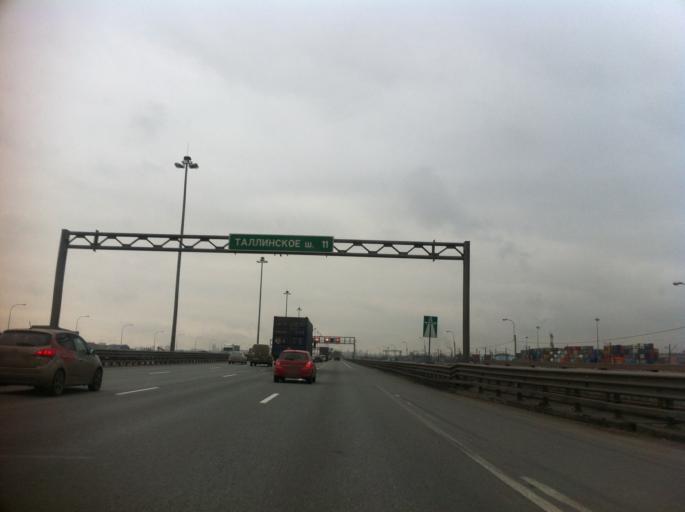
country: RU
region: St.-Petersburg
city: Kupchino
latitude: 59.8159
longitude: 30.3129
